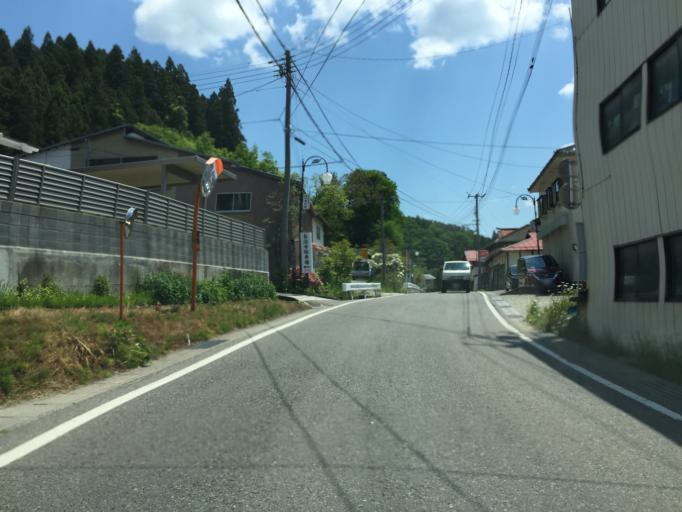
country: JP
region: Fukushima
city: Funehikimachi-funehiki
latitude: 37.5139
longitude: 140.6609
